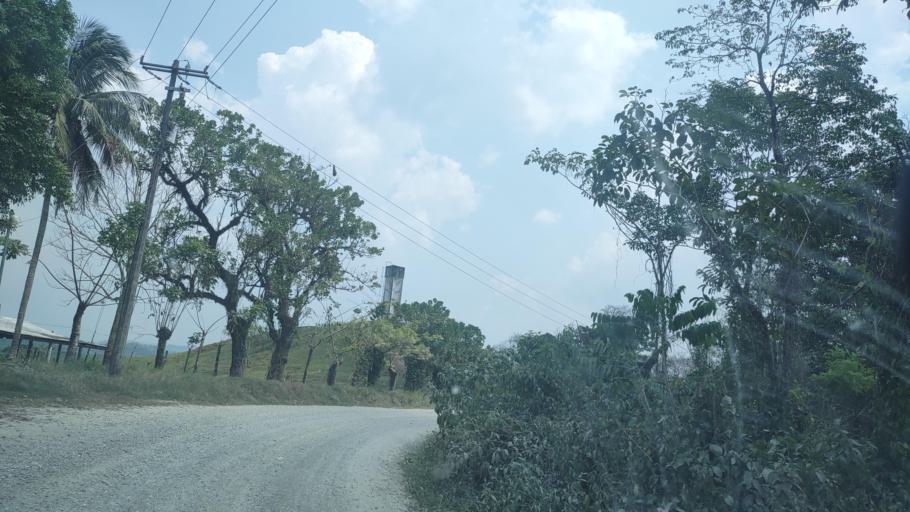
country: MX
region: Tabasco
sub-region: Huimanguillo
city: Francisco Rueda
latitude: 17.6121
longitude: -93.9134
